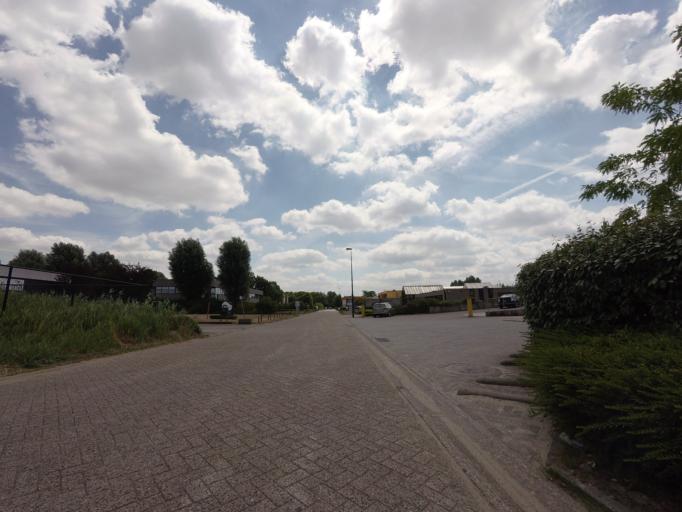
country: BE
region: Flanders
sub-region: Provincie Antwerpen
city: Kontich
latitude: 51.1233
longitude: 4.4581
